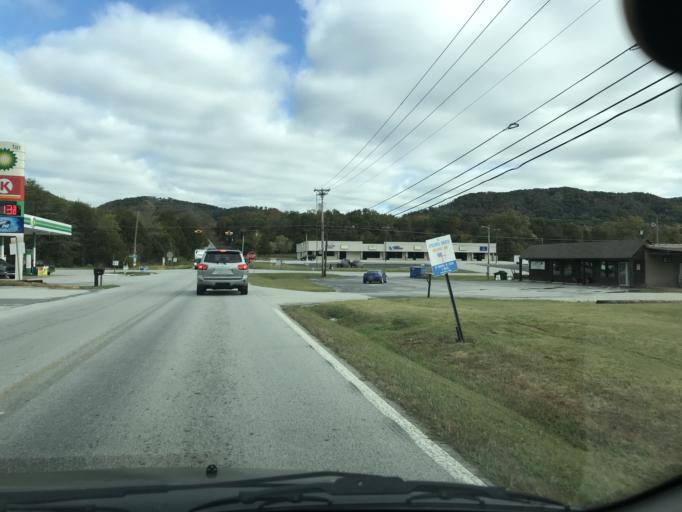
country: US
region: Tennessee
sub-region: Hamilton County
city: Lakesite
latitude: 35.1751
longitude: -85.0286
